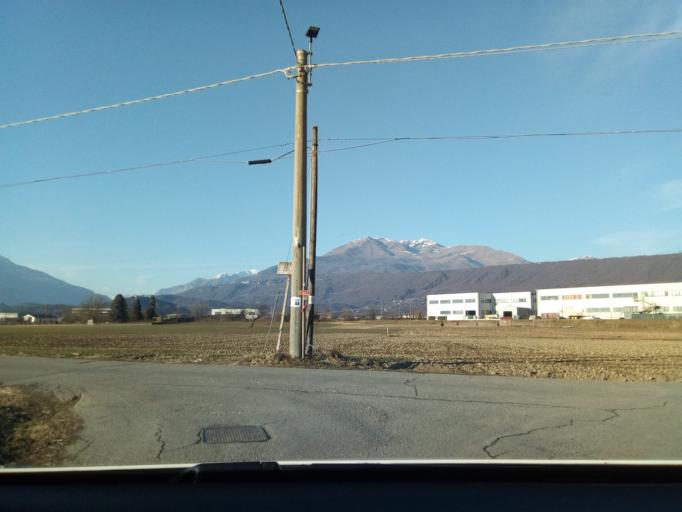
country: IT
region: Piedmont
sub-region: Provincia di Torino
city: Cascinette d'Ivrea
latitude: 45.4661
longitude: 7.9198
